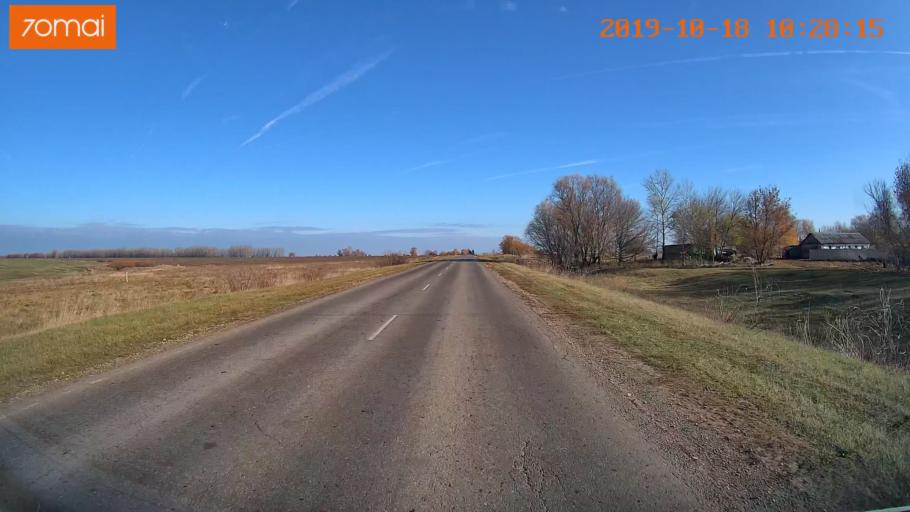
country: RU
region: Tula
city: Kurkino
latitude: 53.4422
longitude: 38.6521
